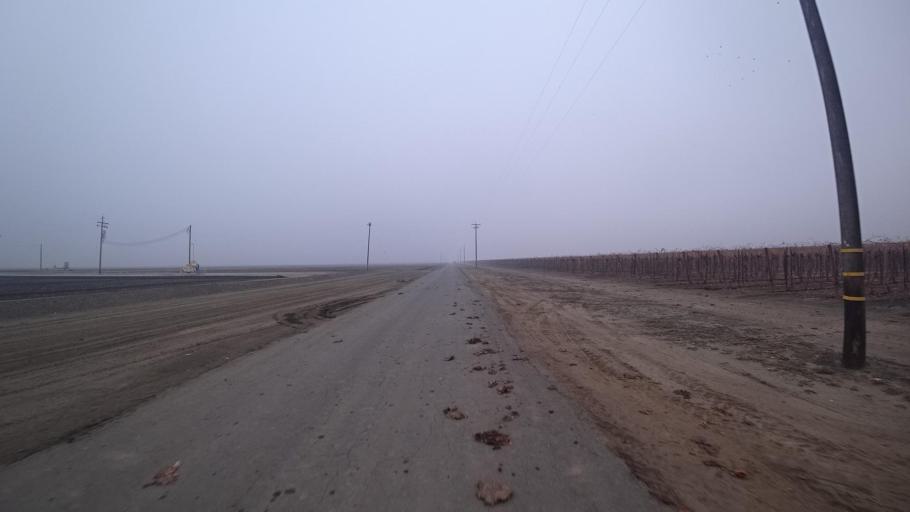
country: US
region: California
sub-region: Kern County
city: Buttonwillow
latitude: 35.4269
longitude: -119.5139
